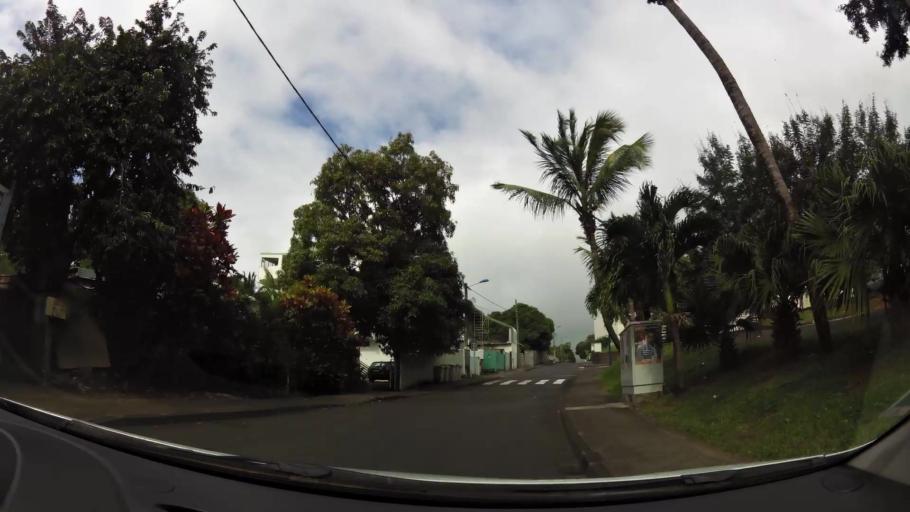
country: RE
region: Reunion
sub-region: Reunion
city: Sainte-Marie
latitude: -20.8984
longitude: 55.5570
